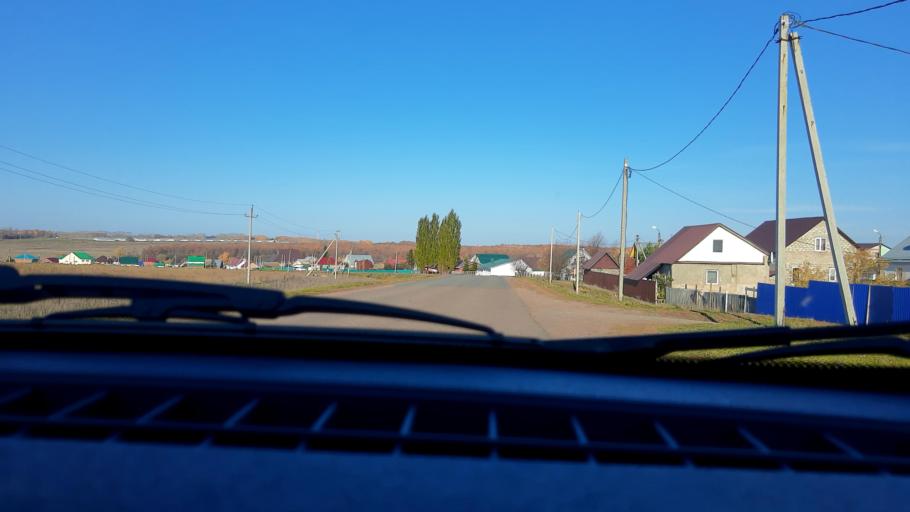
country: RU
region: Bashkortostan
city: Mikhaylovka
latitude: 54.8127
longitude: 55.7878
